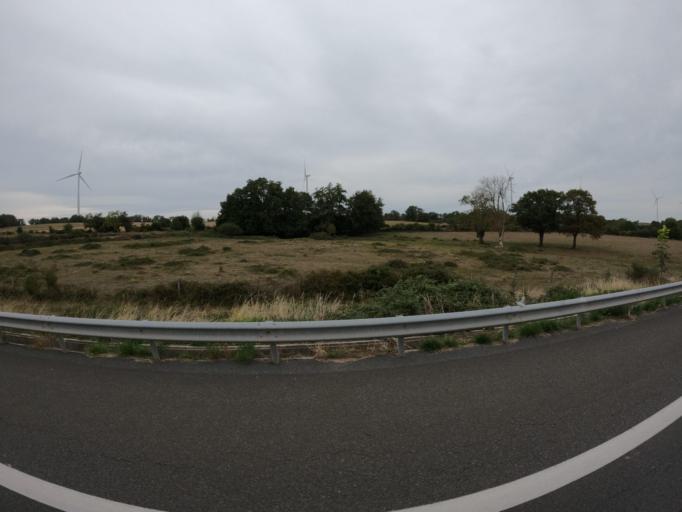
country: FR
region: Auvergne
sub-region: Departement de l'Allier
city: Quinssaines
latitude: 46.3148
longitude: 2.4751
